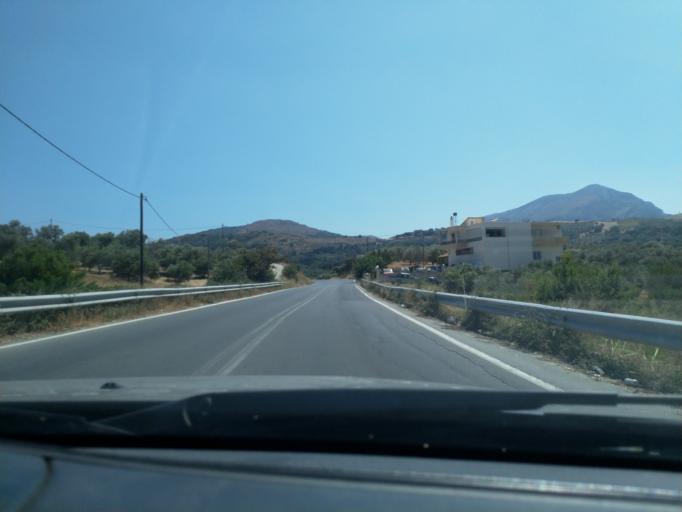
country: GR
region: Crete
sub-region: Nomos Rethymnis
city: Atsipopoulon
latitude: 35.2237
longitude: 24.4855
